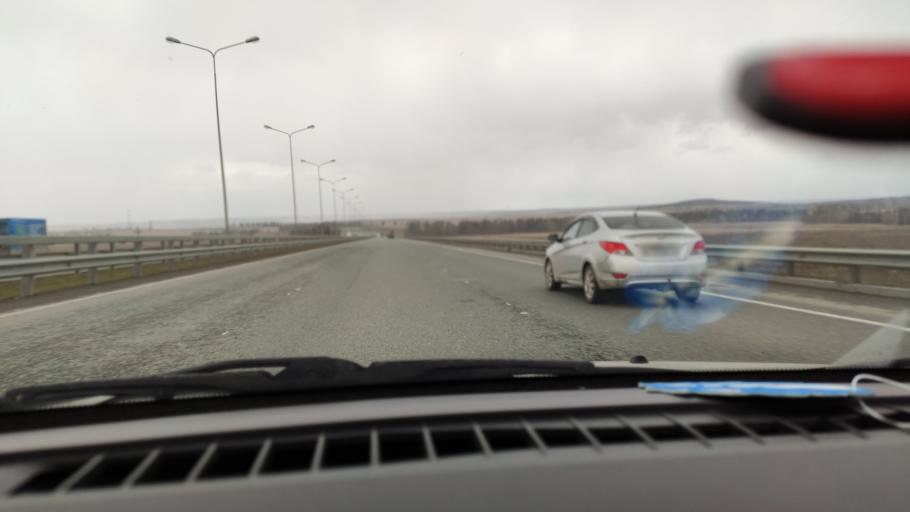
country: RU
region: Perm
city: Zvezdnyy
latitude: 57.7702
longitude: 56.3368
